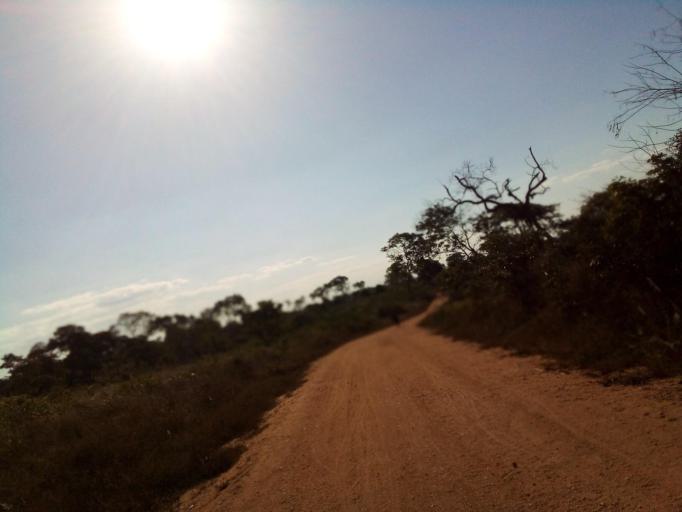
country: MZ
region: Zambezia
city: Quelimane
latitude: -17.5027
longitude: 36.5812
